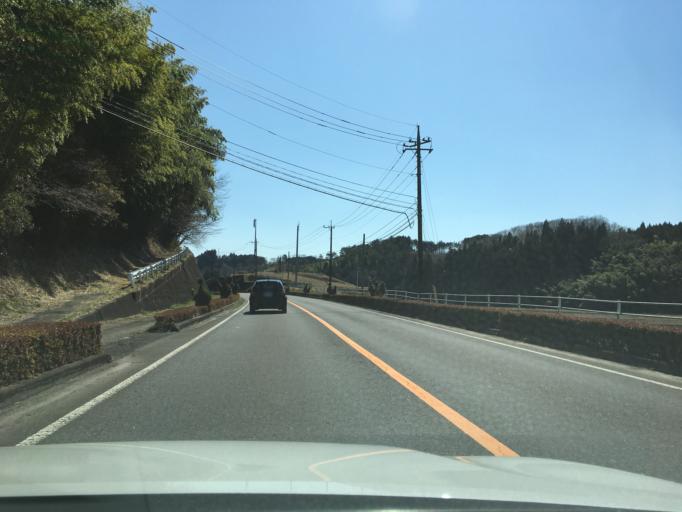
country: JP
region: Tochigi
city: Kuroiso
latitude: 37.0325
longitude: 140.1732
